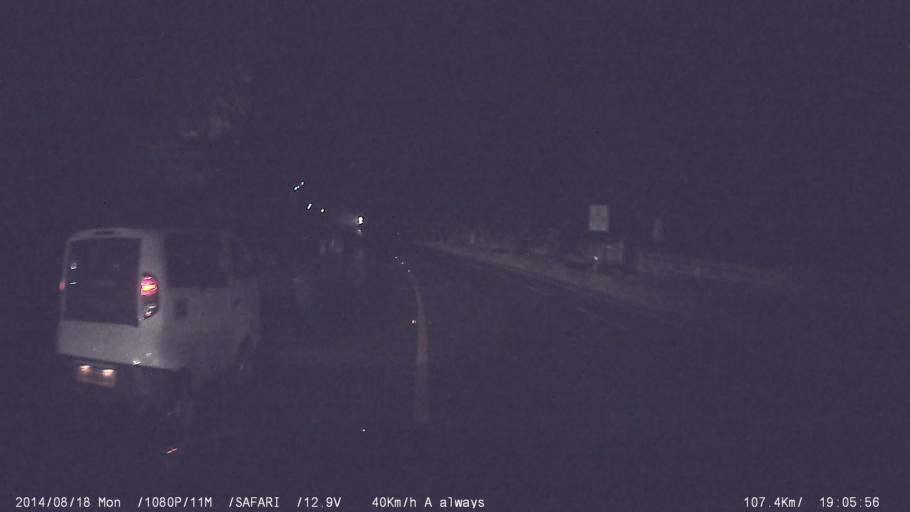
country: IN
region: Kerala
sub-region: Ernakulam
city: Perumbavoor
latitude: 10.0610
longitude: 76.5230
